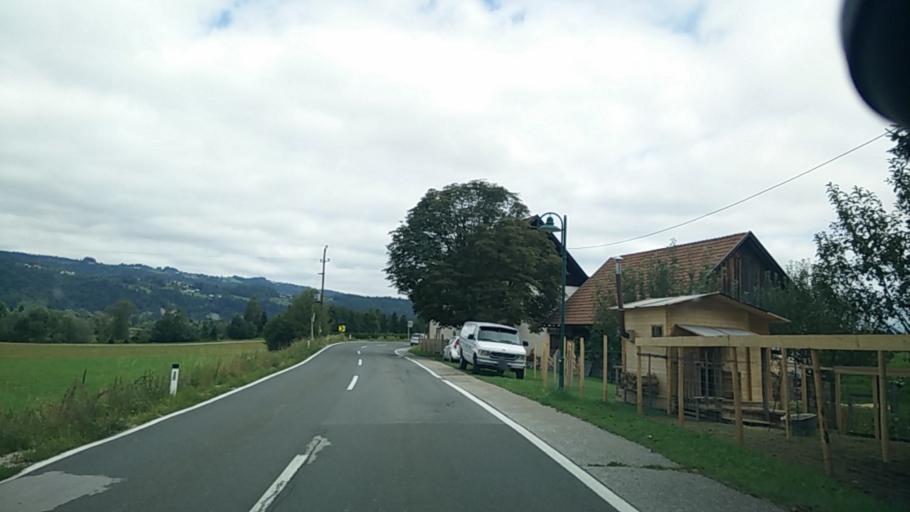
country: AT
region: Carinthia
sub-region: Politischer Bezirk Klagenfurt Land
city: Kottmannsdorf
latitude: 46.5305
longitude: 14.2128
